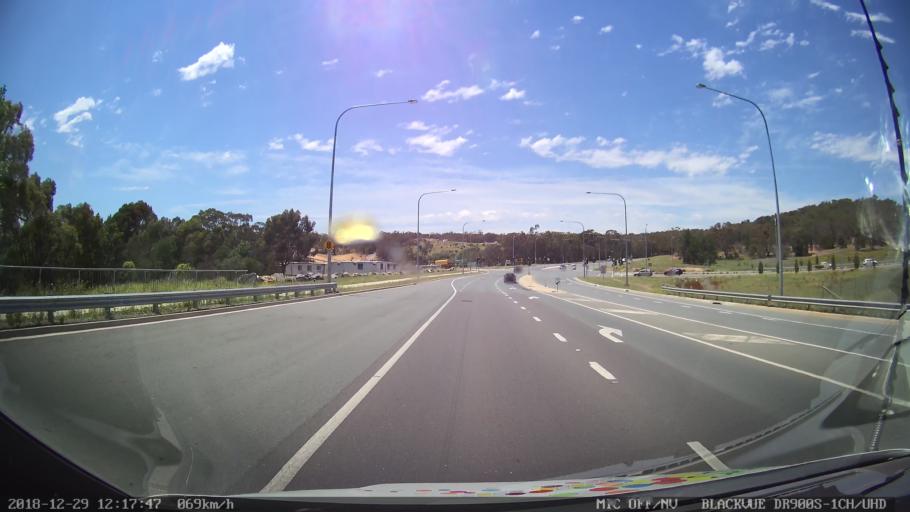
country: AU
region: New South Wales
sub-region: Queanbeyan
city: Queanbeyan
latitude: -35.3780
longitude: 149.2351
